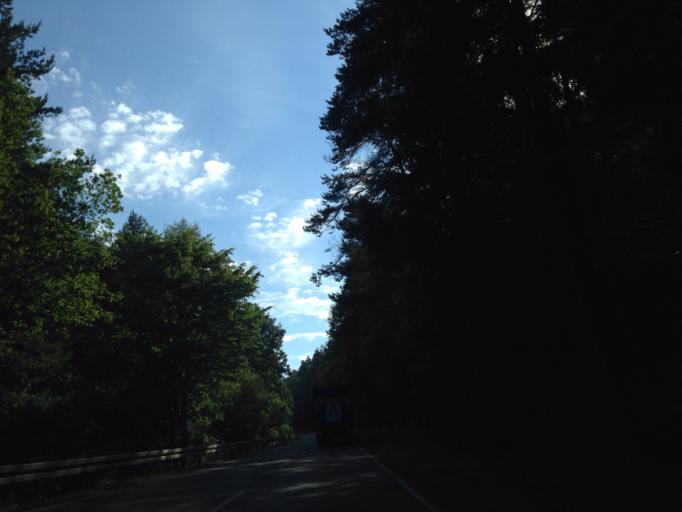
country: DE
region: Thuringia
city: Schwarza
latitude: 50.7999
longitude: 11.3178
